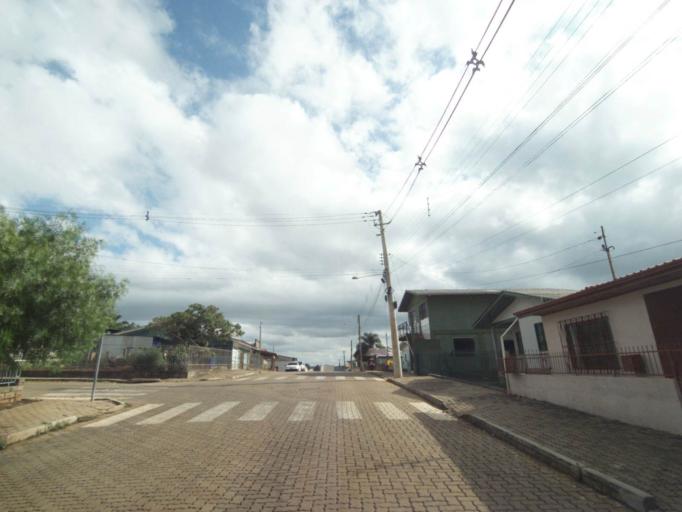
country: BR
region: Rio Grande do Sul
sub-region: Lagoa Vermelha
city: Lagoa Vermelha
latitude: -28.1993
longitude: -51.5275
